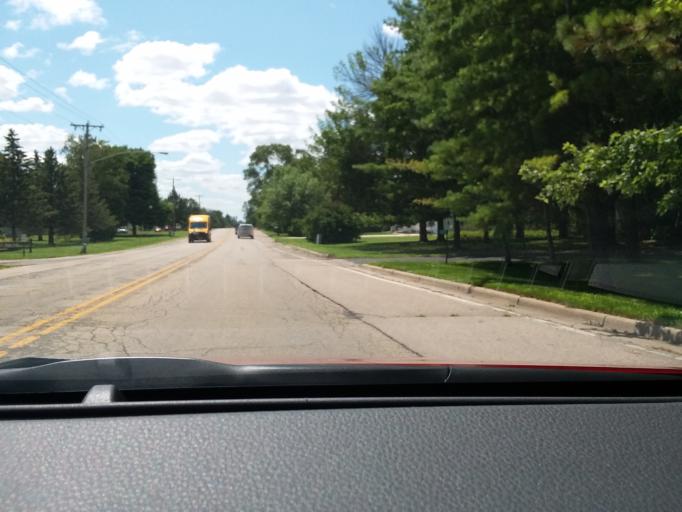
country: US
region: Wisconsin
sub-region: Dane County
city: Windsor
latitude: 43.2088
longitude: -89.3431
